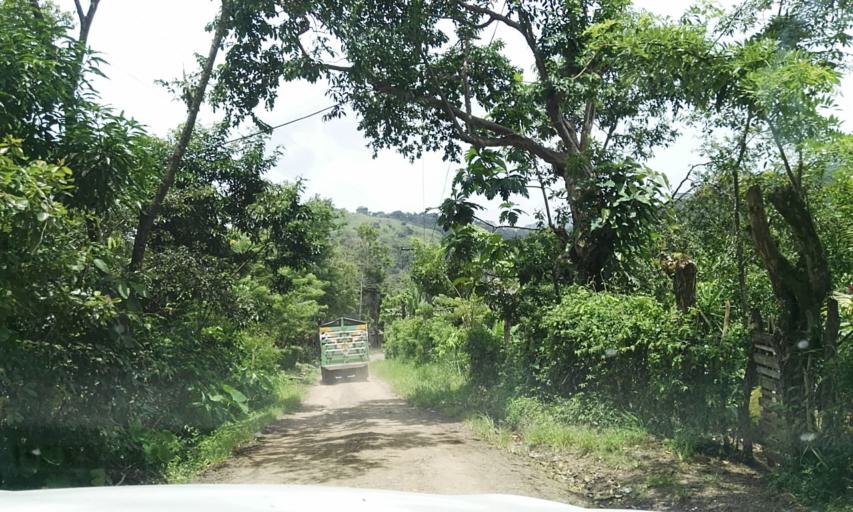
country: NI
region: Matagalpa
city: San Ramon
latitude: 12.9824
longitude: -85.8434
